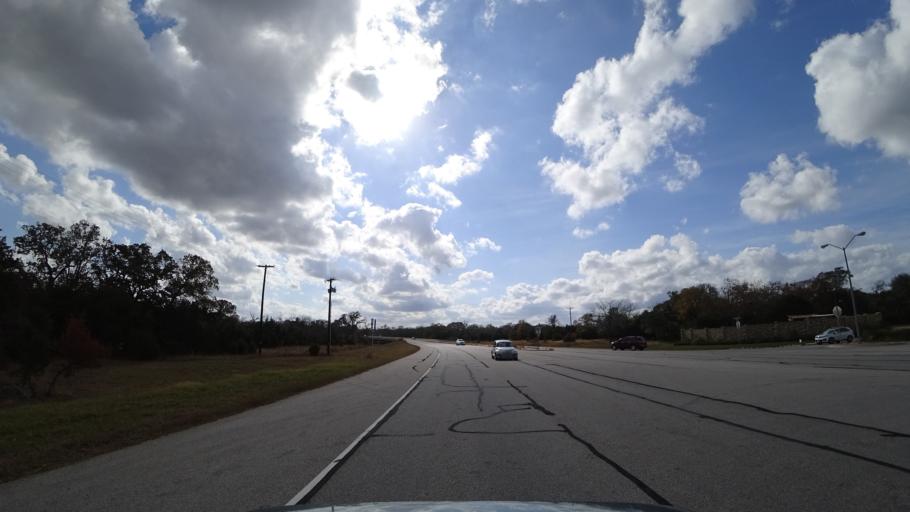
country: US
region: Texas
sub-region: Williamson County
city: Brushy Creek
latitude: 30.4875
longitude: -97.7193
